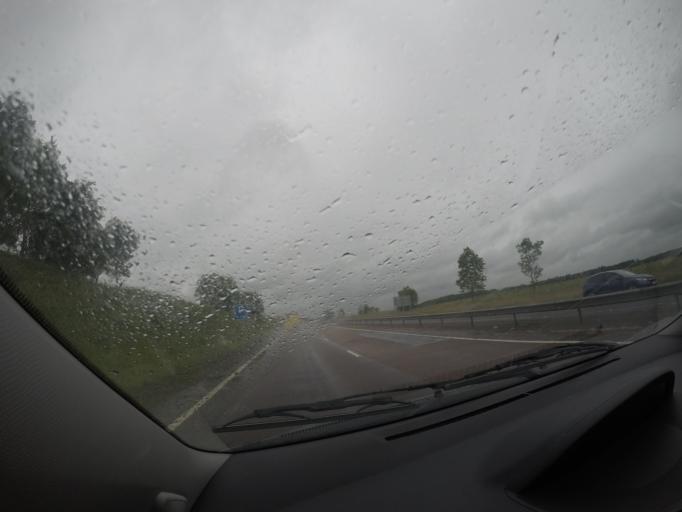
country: GB
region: Scotland
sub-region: Angus
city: Forfar
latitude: 56.6823
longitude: -2.8625
